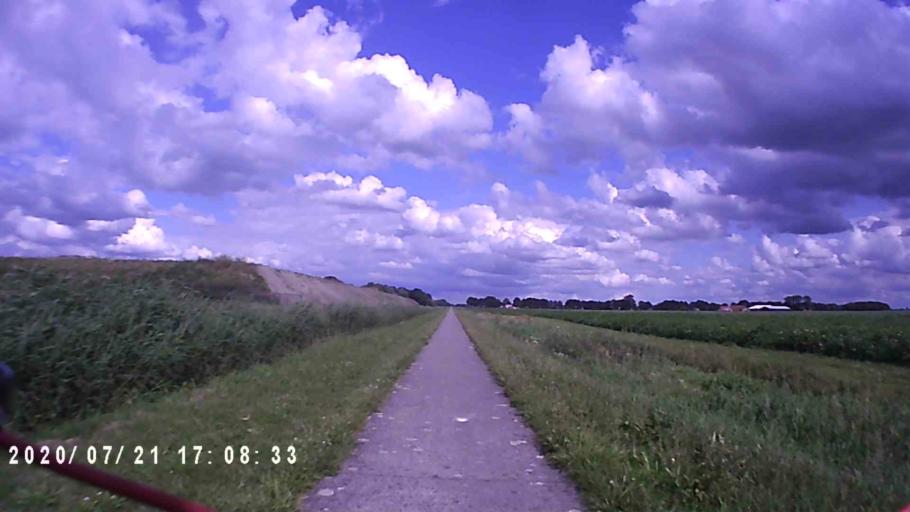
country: NL
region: Groningen
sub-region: Gemeente Hoogezand-Sappemeer
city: Hoogezand
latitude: 53.1299
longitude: 6.7468
